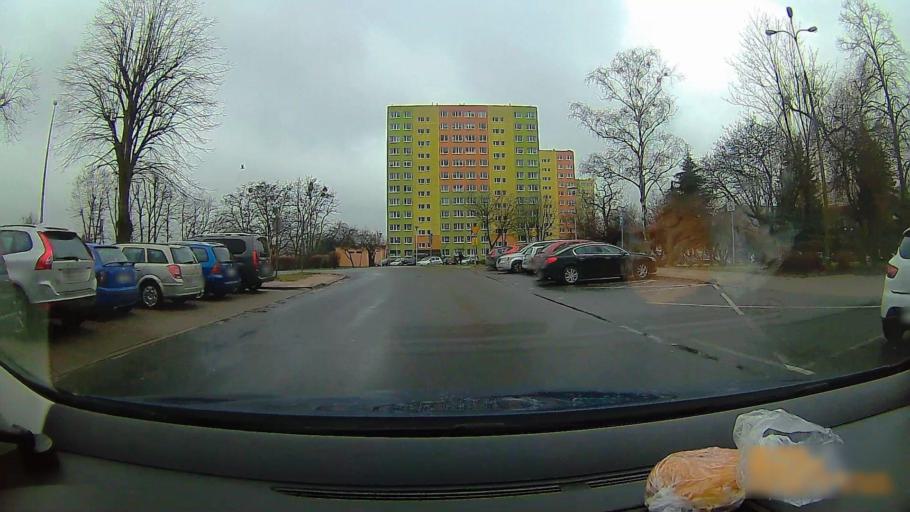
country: PL
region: Greater Poland Voivodeship
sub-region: Konin
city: Konin
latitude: 52.2268
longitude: 18.2522
